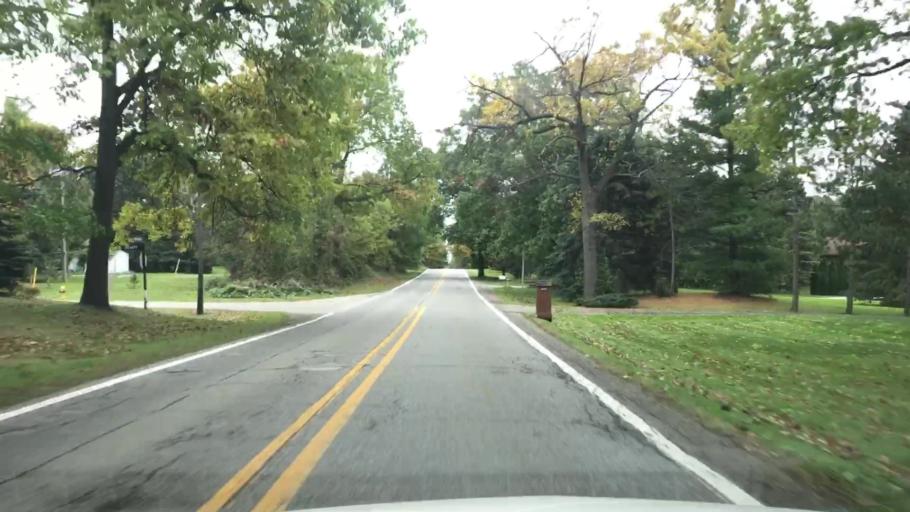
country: US
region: Michigan
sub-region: Macomb County
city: Shelby
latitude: 42.7386
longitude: -83.0567
